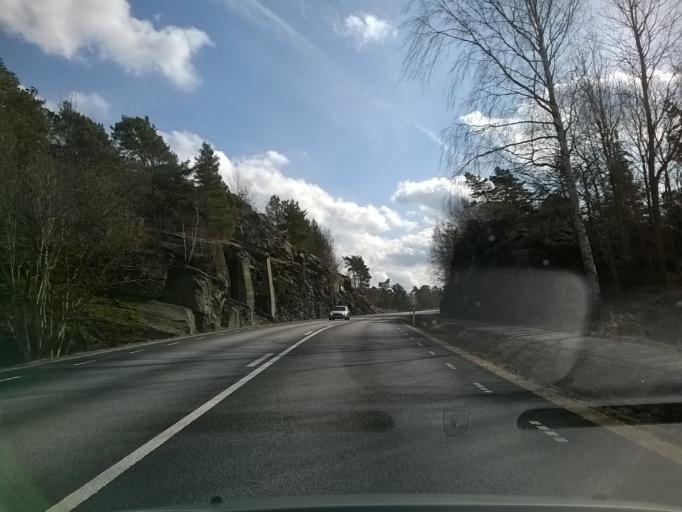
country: SE
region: Vaestra Goetaland
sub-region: Orust
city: Henan
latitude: 58.3108
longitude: 11.6955
